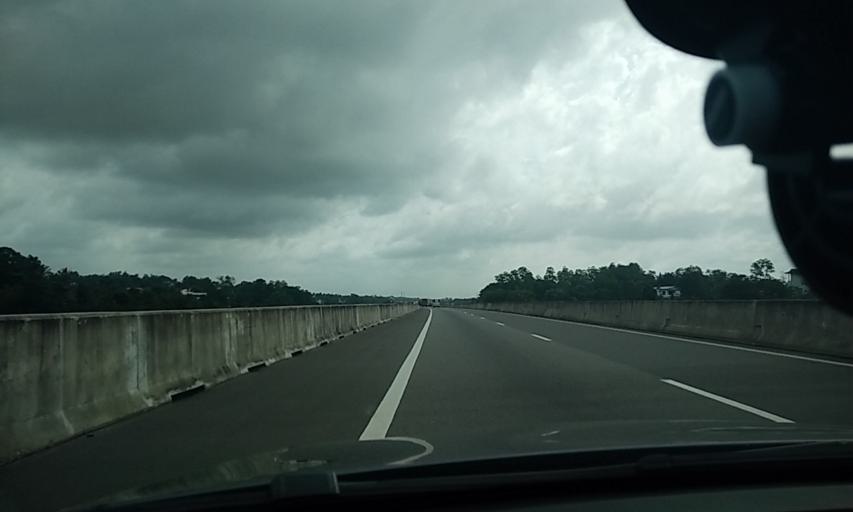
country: LK
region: Western
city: Homagama
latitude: 6.8947
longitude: 79.9784
